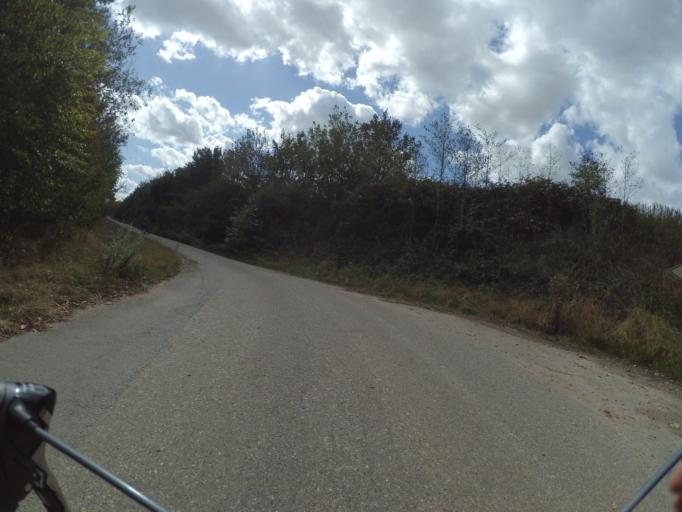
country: DE
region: North Rhine-Westphalia
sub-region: Regierungsbezirk Koln
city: Inden
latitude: 50.8761
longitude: 6.3918
